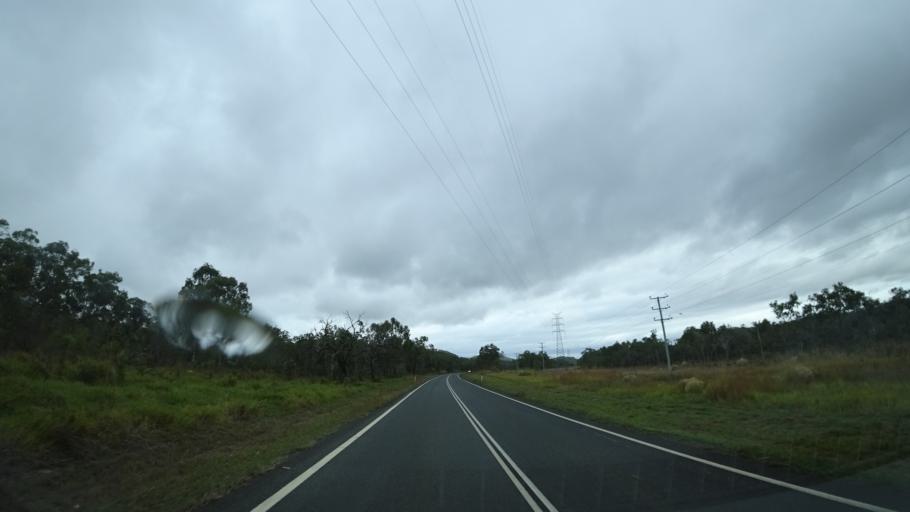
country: AU
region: Queensland
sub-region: Cairns
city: Port Douglas
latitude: -16.7172
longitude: 145.3527
